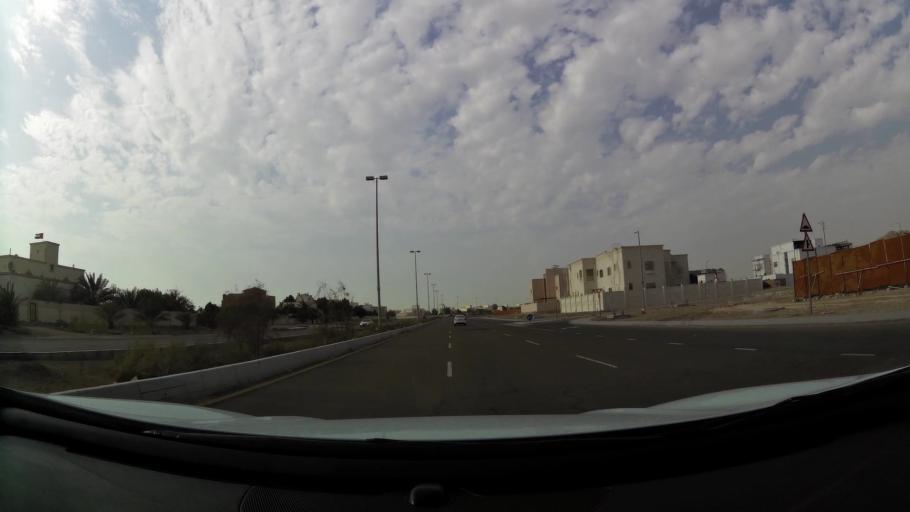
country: AE
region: Abu Dhabi
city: Abu Dhabi
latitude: 24.3422
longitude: 54.5680
